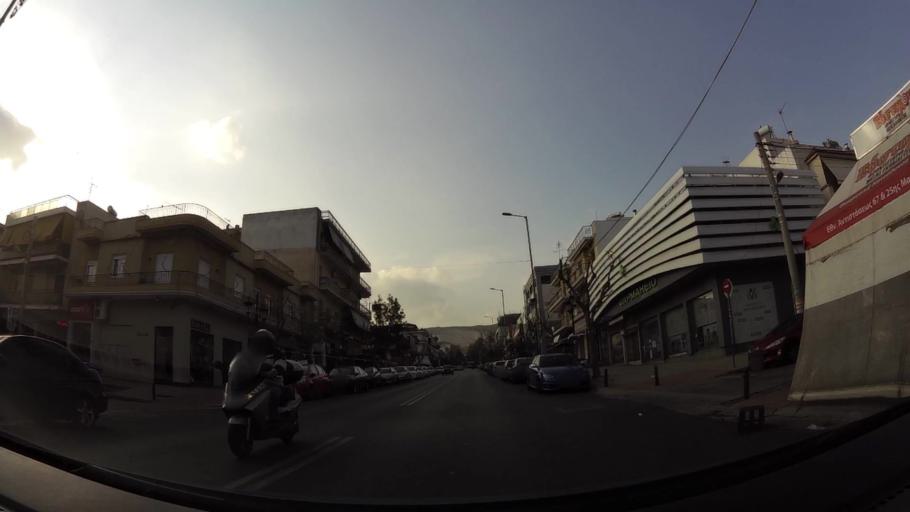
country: GR
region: Attica
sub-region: Nomarchia Athinas
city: Petroupolis
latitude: 38.0408
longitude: 23.6874
